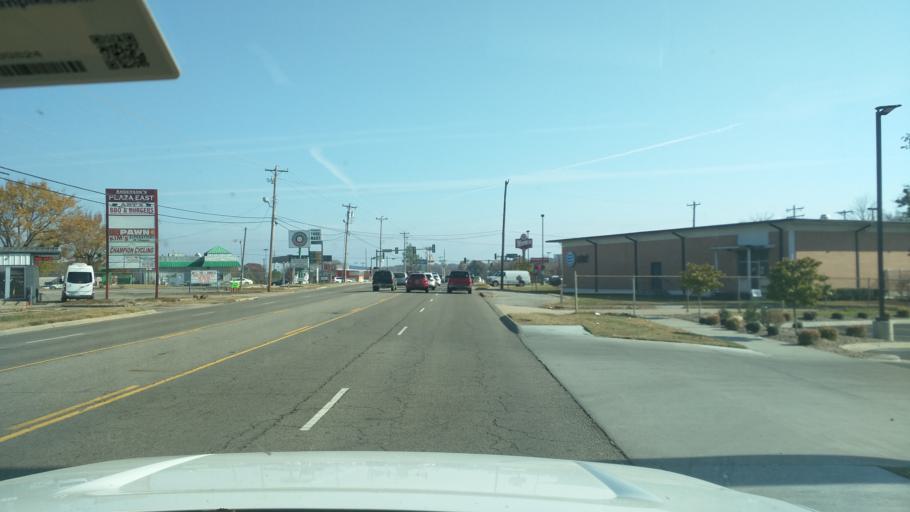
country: US
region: Arkansas
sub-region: Sebastian County
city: Barling
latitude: 35.3490
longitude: -94.3424
